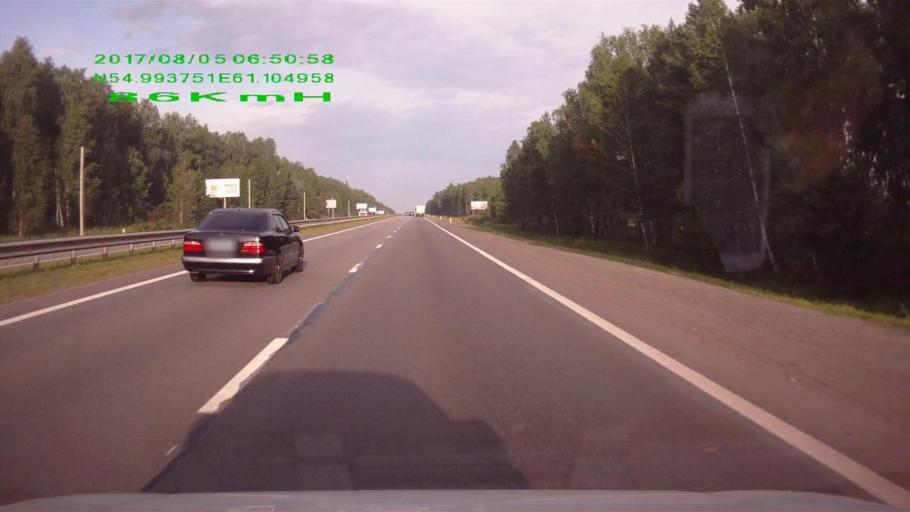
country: RU
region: Chelyabinsk
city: Poletayevo
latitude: 54.9937
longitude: 61.1047
